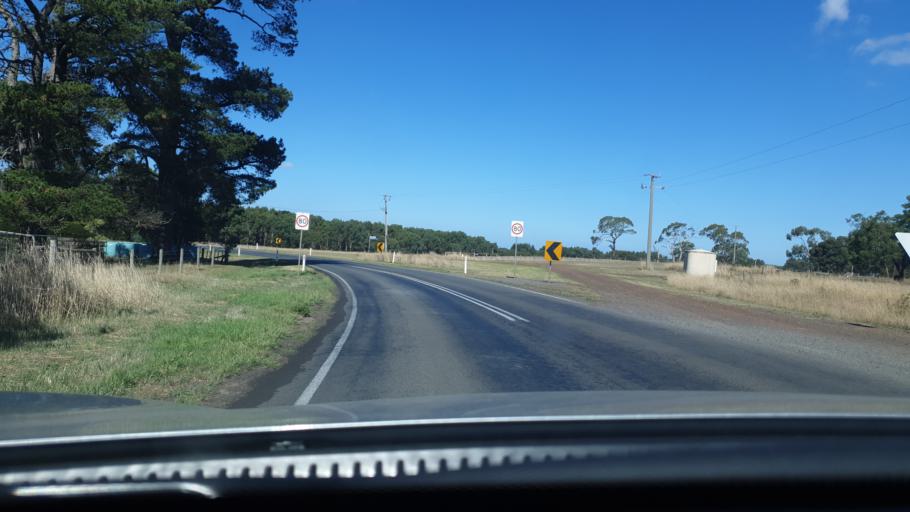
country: AU
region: Victoria
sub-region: Warrnambool
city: Warrnambool
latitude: -38.1832
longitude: 142.4254
